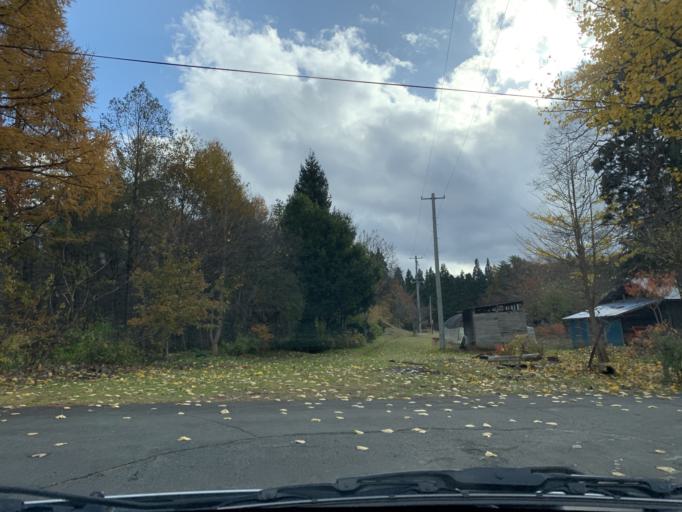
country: JP
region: Iwate
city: Mizusawa
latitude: 39.1030
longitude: 140.9774
